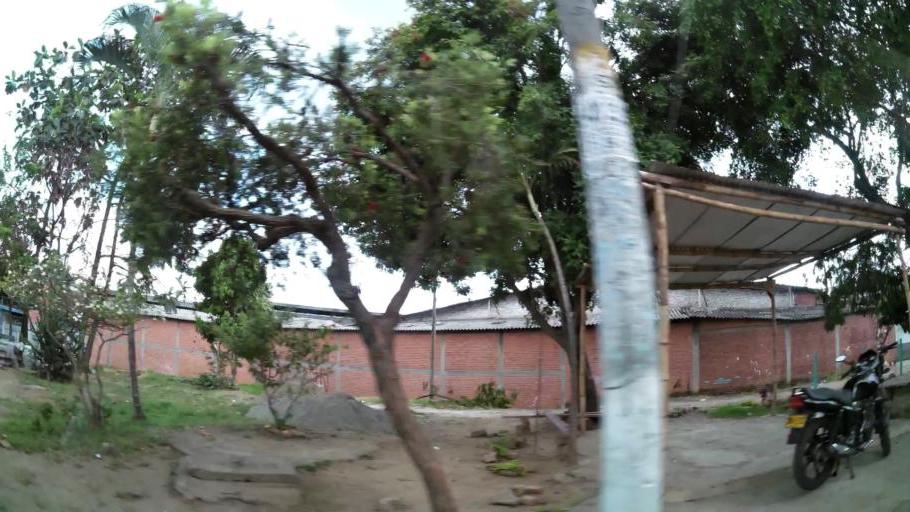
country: CO
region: Valle del Cauca
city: Cali
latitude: 3.4817
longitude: -76.5061
